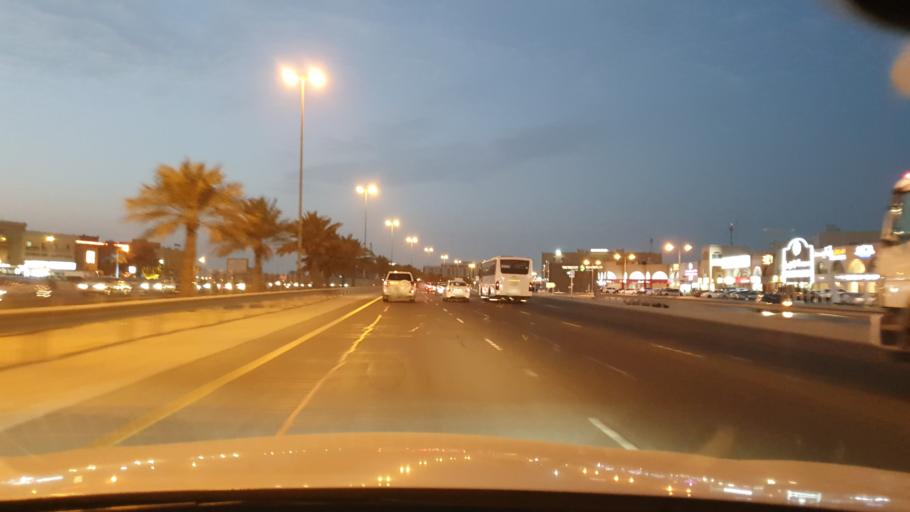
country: BH
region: Northern
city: Ar Rifa'
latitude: 26.1423
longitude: 50.5797
